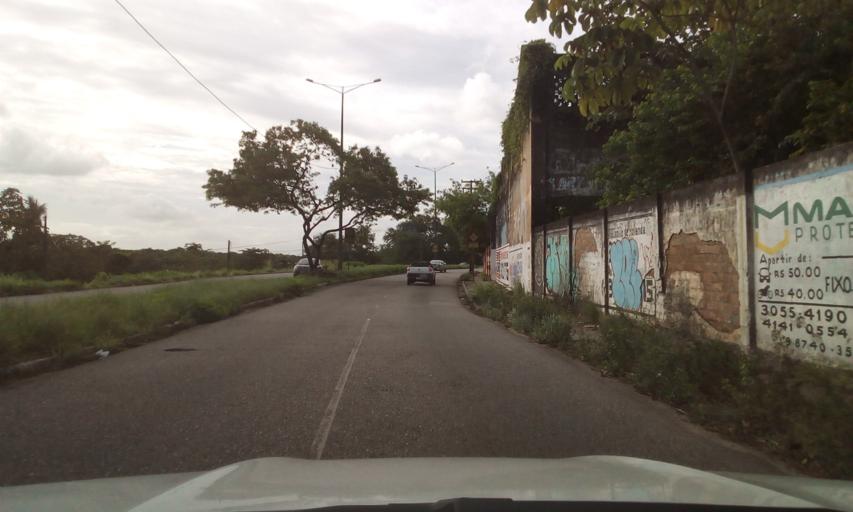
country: BR
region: Paraiba
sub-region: Joao Pessoa
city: Joao Pessoa
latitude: -7.1221
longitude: -34.8931
